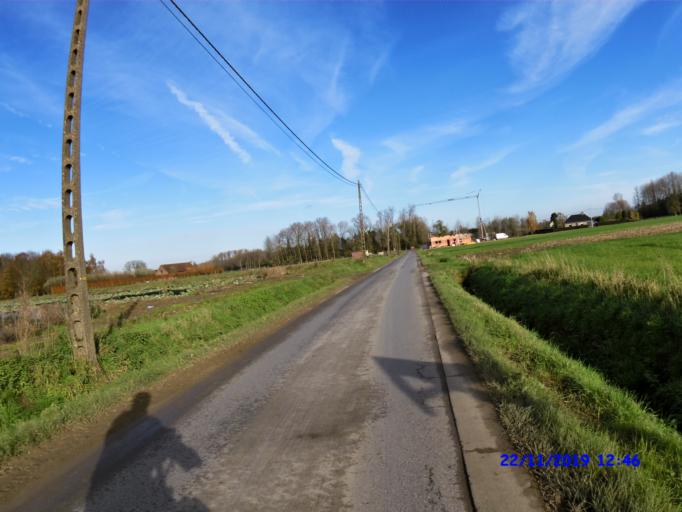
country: BE
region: Flanders
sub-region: Provincie Vlaams-Brabant
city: Merchtem
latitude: 50.9654
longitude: 4.2690
